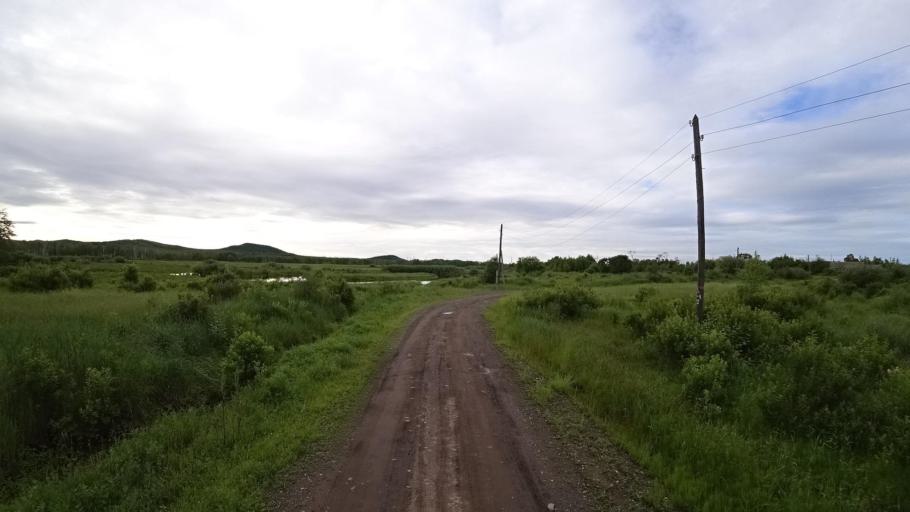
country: RU
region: Khabarovsk Krai
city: Amursk
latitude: 49.8849
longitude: 136.1286
